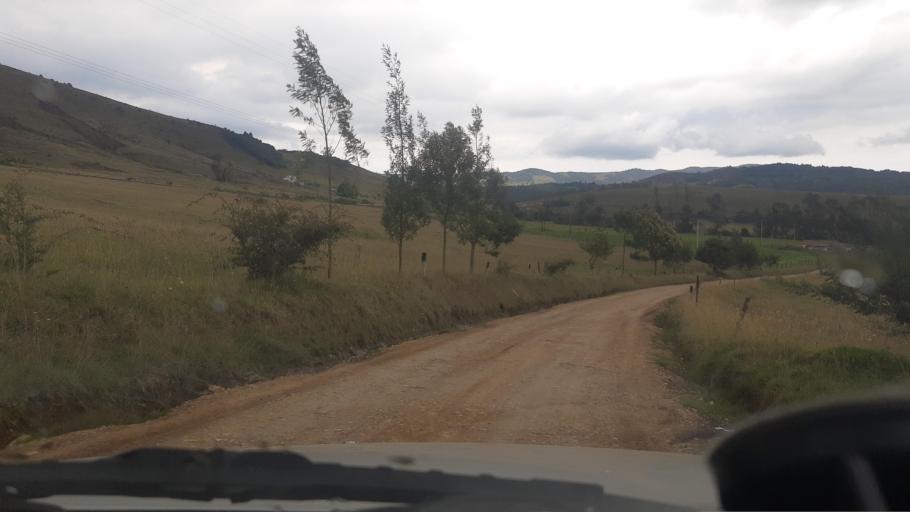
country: CO
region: Cundinamarca
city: Suesca
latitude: 5.1674
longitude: -73.8023
